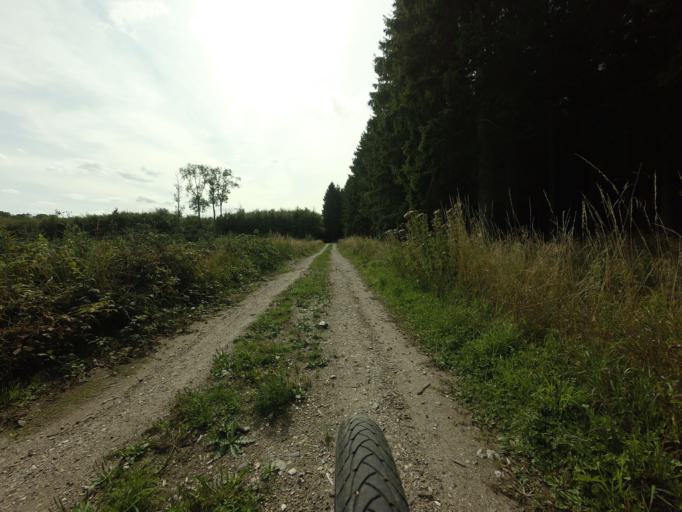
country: DK
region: Zealand
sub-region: Faxe Kommune
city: Fakse Ladeplads
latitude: 55.2320
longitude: 12.1857
